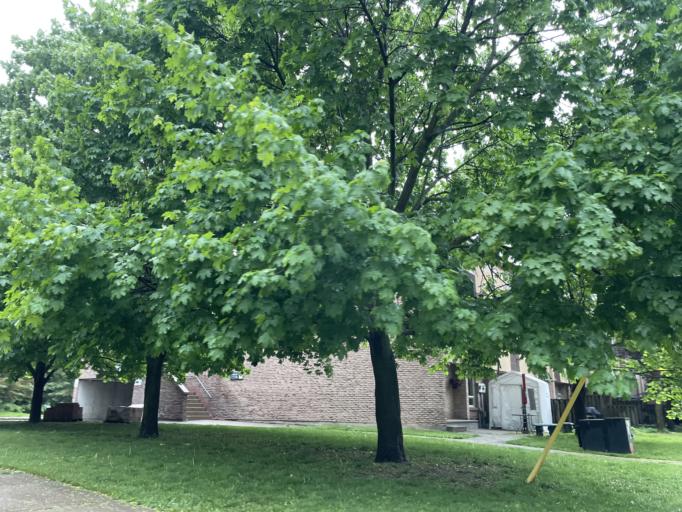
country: CA
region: Ontario
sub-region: Wellington County
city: Guelph
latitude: 43.5582
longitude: -80.2799
